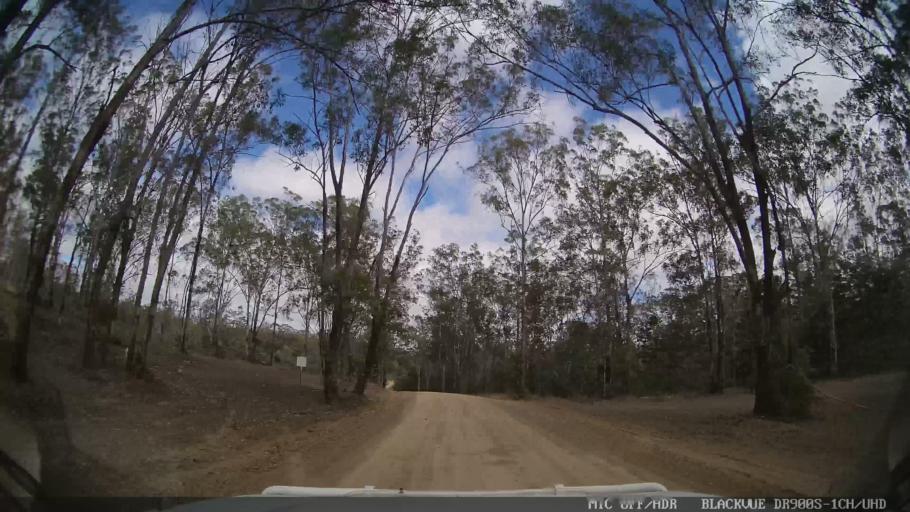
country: AU
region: Queensland
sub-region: Gladstone
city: Toolooa
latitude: -24.6829
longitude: 151.3313
